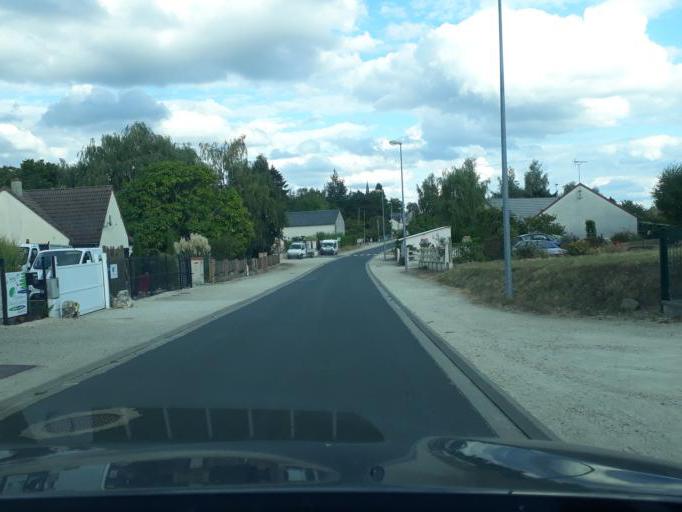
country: FR
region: Centre
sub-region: Departement du Loiret
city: Loury
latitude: 48.0022
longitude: 2.0801
